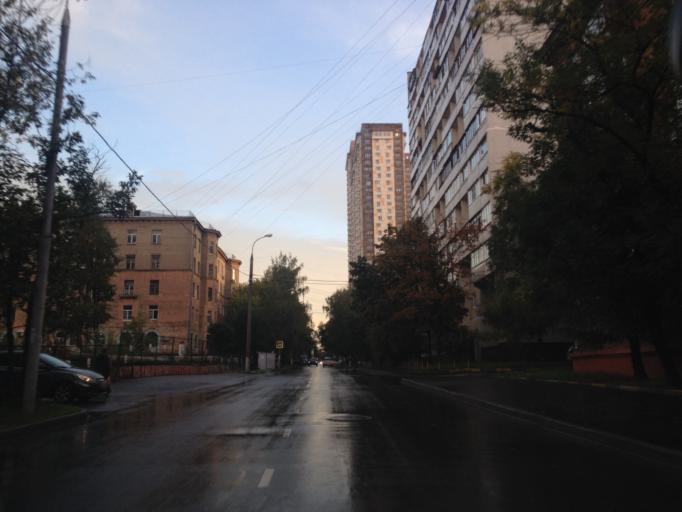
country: RU
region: Moscow
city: Metrogorodok
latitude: 55.7956
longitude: 37.7881
